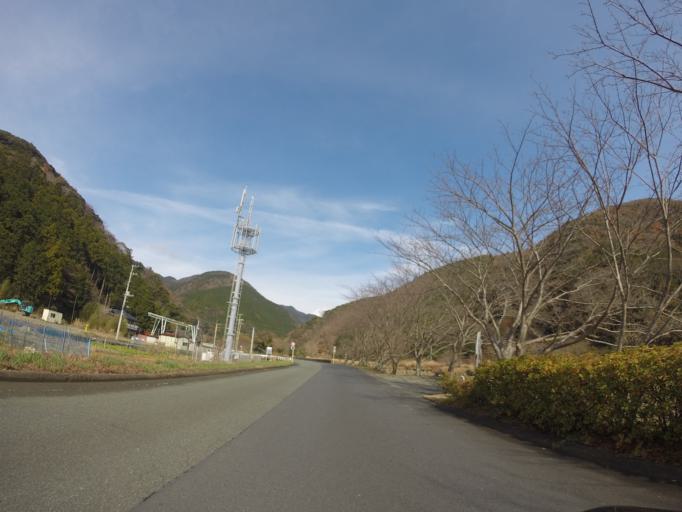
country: JP
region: Shizuoka
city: Heda
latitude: 34.7868
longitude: 138.8011
